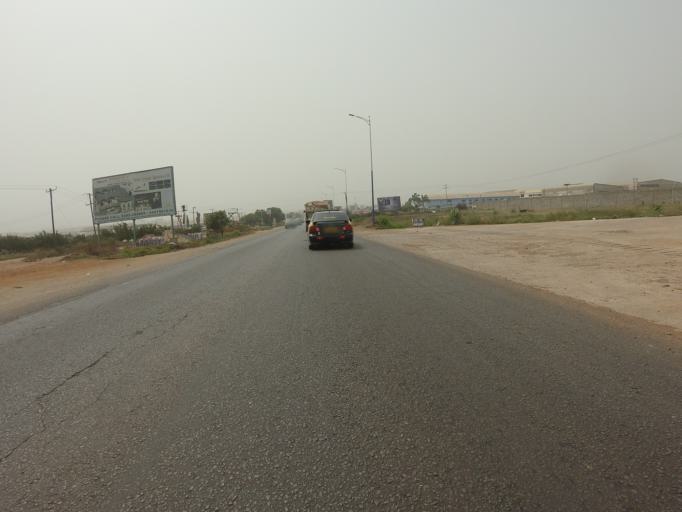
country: GH
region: Greater Accra
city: Tema
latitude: 5.7264
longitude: 0.0232
